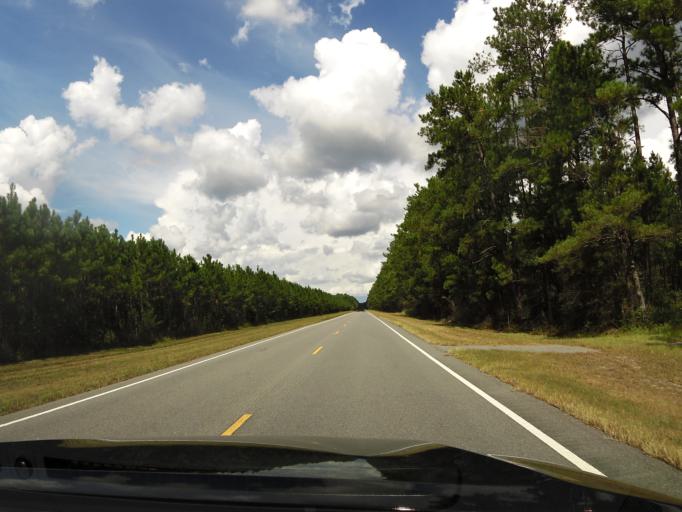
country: US
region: Georgia
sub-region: Charlton County
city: Folkston
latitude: 30.9928
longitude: -82.0262
